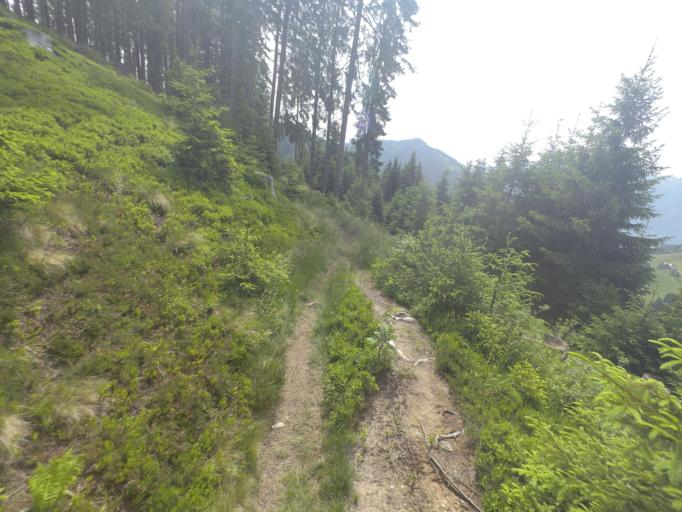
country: AT
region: Salzburg
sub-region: Politischer Bezirk Sankt Johann im Pongau
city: Muhlbach am Hochkonig
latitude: 47.3634
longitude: 13.1041
